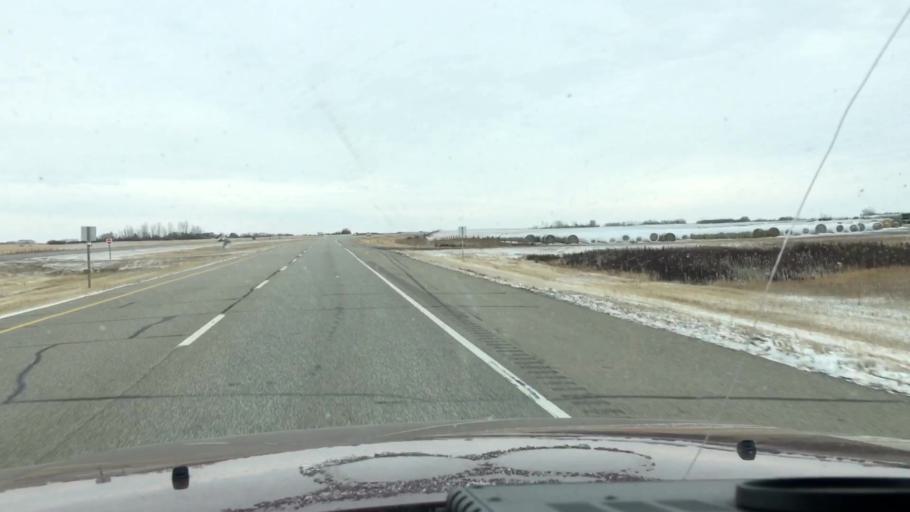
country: CA
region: Saskatchewan
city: Watrous
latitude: 51.3657
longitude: -106.1317
